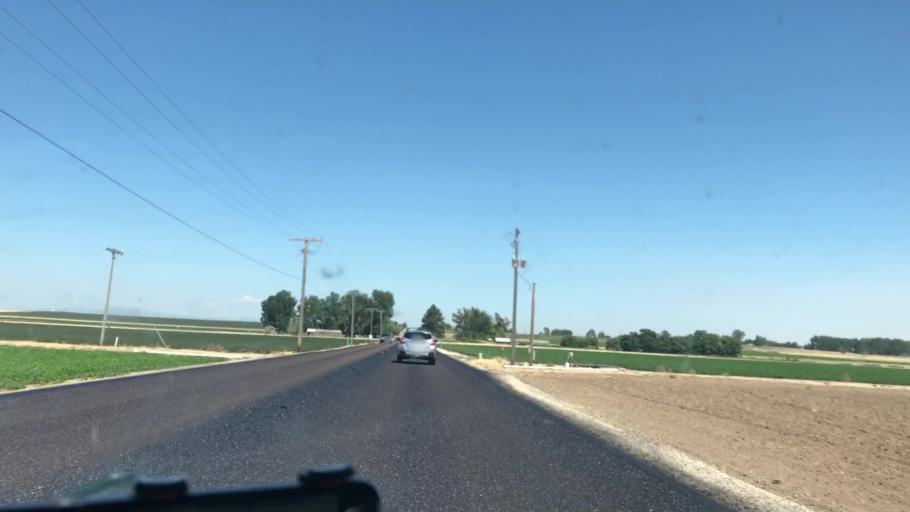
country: US
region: Idaho
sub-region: Canyon County
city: Caldwell
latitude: 43.6036
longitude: -116.7389
